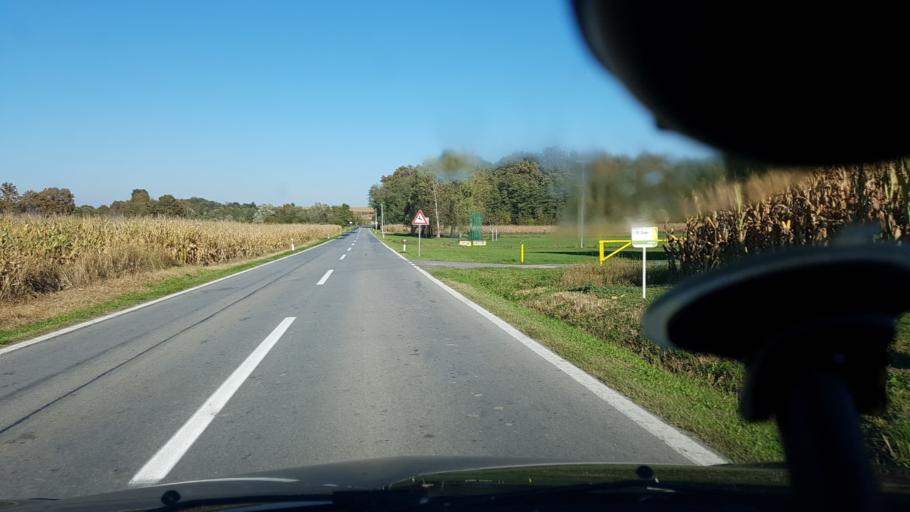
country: HR
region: Bjelovarsko-Bilogorska
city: Gudovac
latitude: 45.8278
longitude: 16.7497
